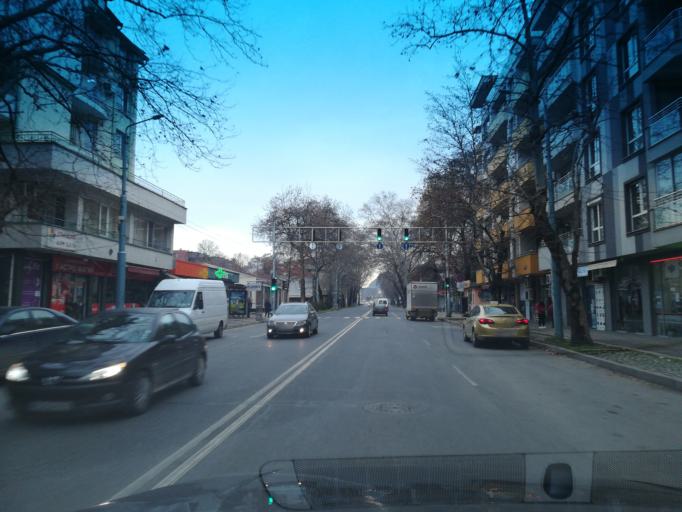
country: BG
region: Plovdiv
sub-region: Obshtina Plovdiv
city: Plovdiv
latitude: 42.1362
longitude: 24.7583
